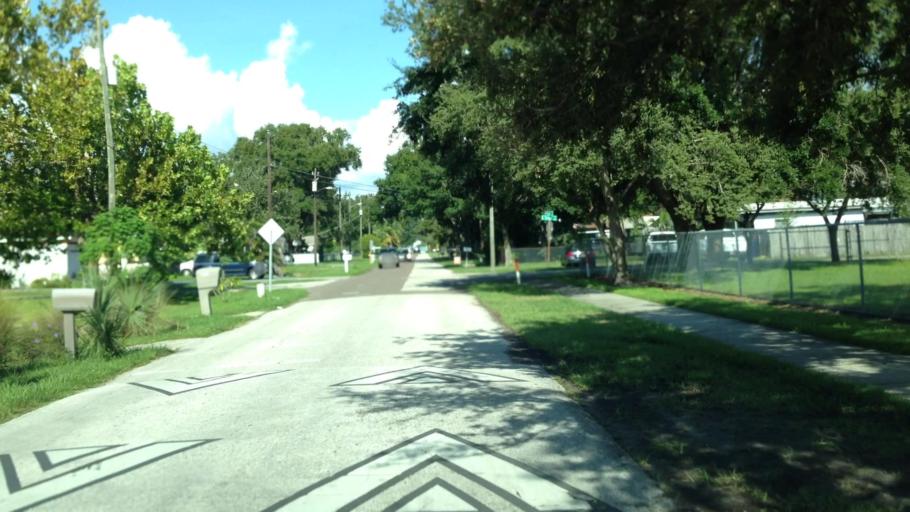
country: US
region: Florida
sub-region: Hillsborough County
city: Tampa
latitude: 27.8877
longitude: -82.5223
